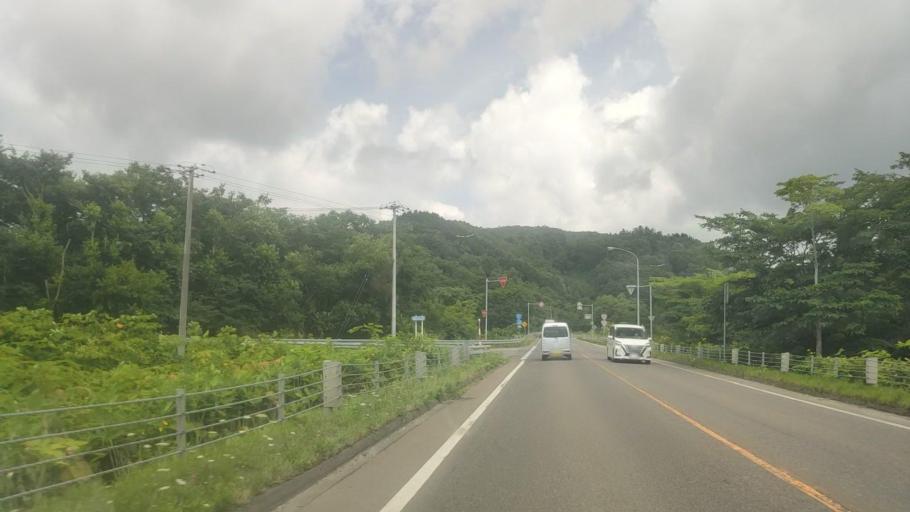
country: JP
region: Hokkaido
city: Niseko Town
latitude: 42.5908
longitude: 140.4510
